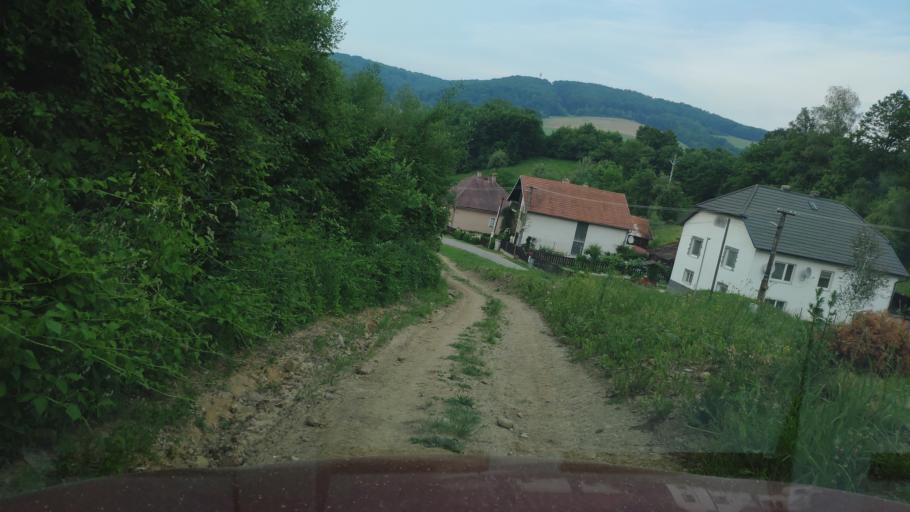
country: SK
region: Presovsky
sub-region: Okres Presov
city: Presov
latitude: 48.9582
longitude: 21.1396
